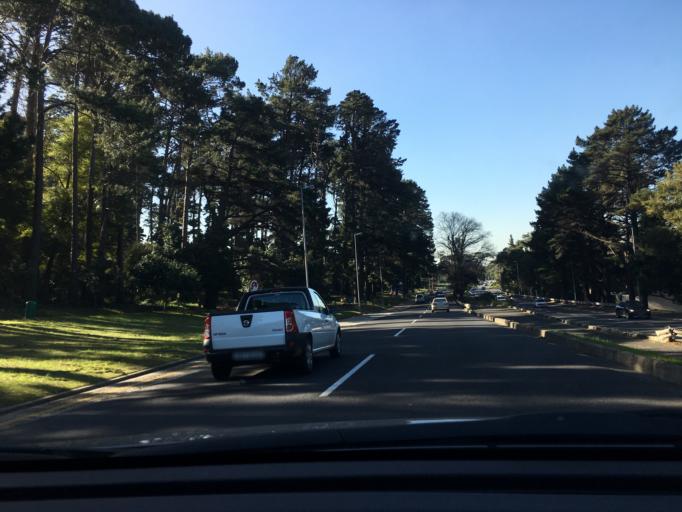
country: ZA
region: Western Cape
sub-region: City of Cape Town
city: Newlands
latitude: -33.9679
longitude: 18.4551
